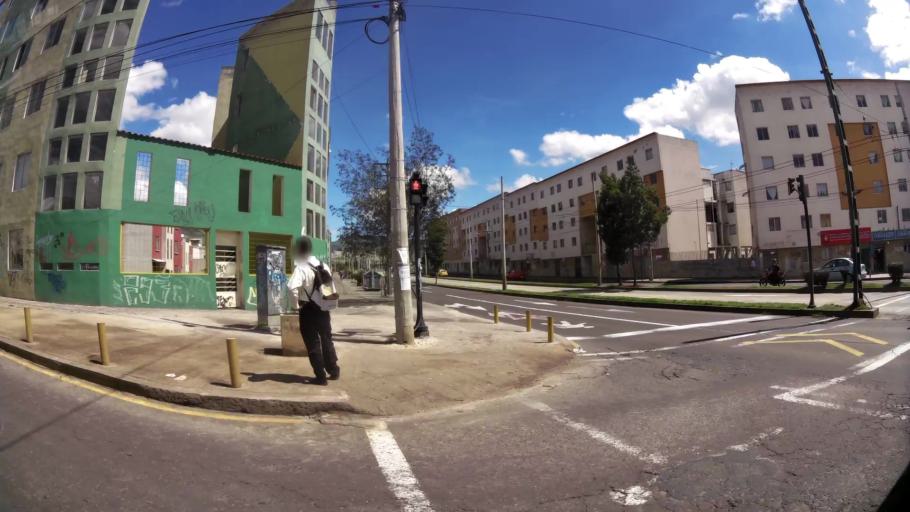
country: EC
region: Pichincha
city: Quito
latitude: -0.2968
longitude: -78.5530
